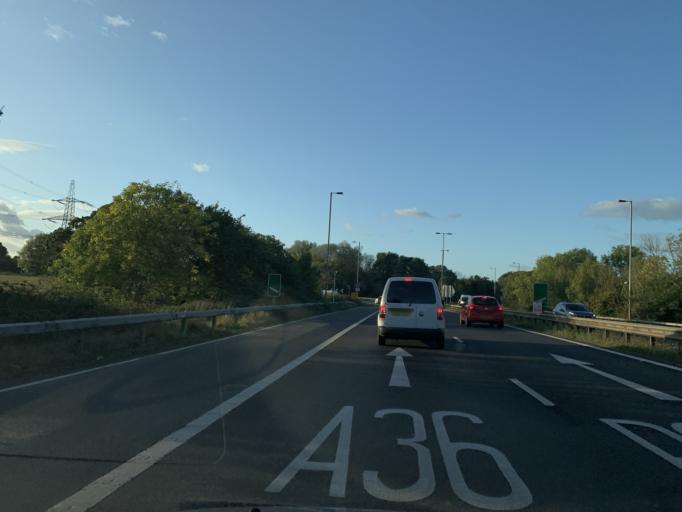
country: GB
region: England
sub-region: Hampshire
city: Romsey
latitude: 50.9527
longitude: -1.5333
